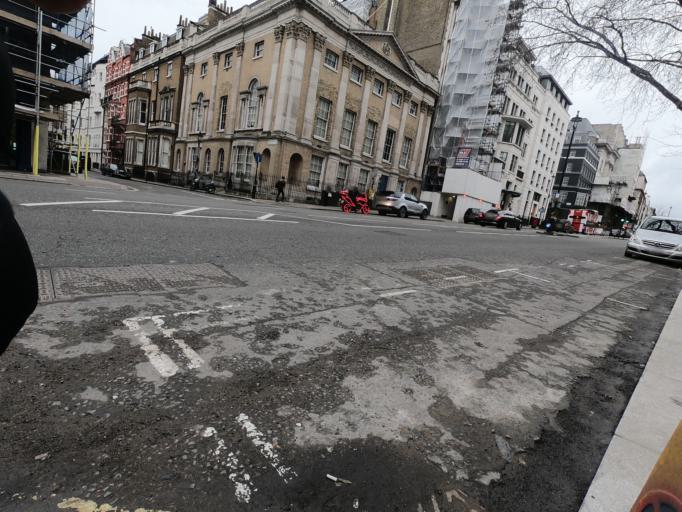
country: GB
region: England
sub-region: Greater London
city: London
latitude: 51.5066
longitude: -0.1394
